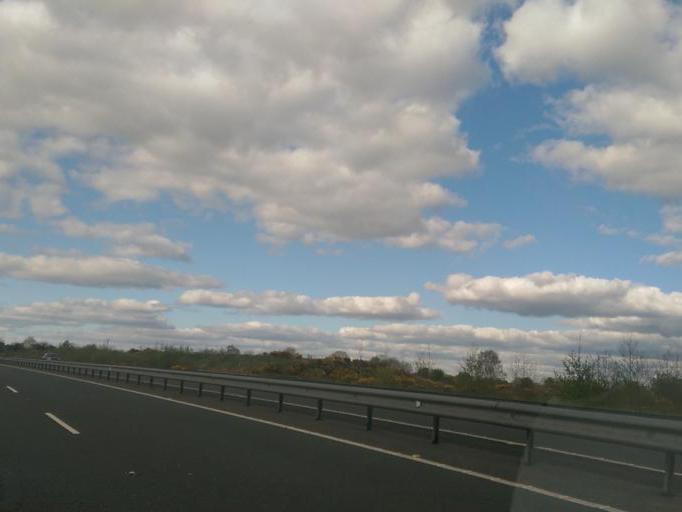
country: IE
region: Leinster
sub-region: An Iarmhi
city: Athlone
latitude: 53.3569
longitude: -8.0638
